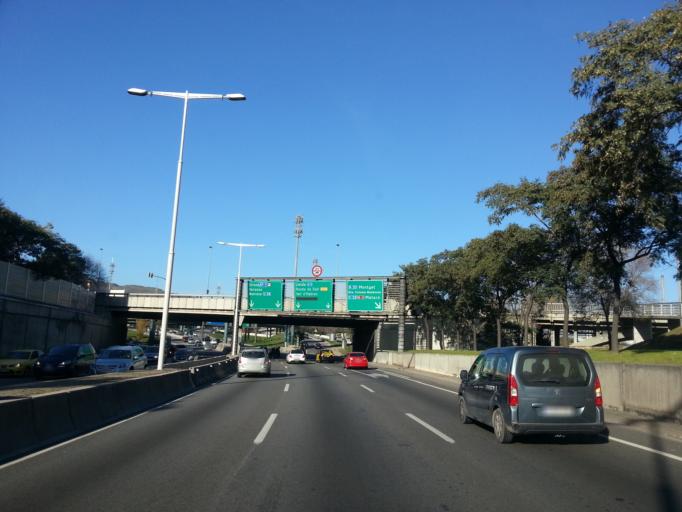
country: ES
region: Catalonia
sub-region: Provincia de Barcelona
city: Santa Coloma de Gramenet
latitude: 41.4484
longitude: 2.2017
